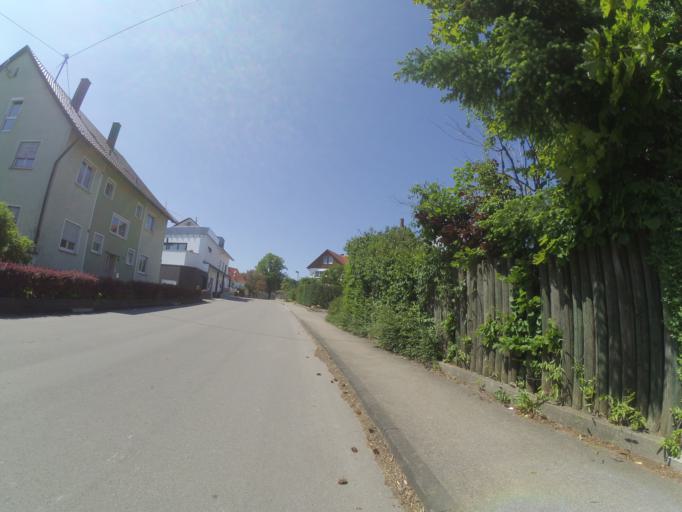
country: DE
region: Baden-Wuerttemberg
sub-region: Tuebingen Region
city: Merklingen
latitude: 48.5076
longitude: 9.7556
